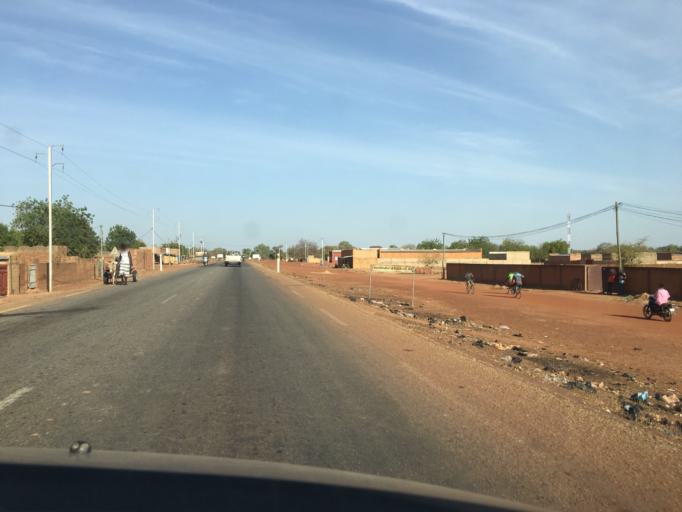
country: BF
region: Plateau-Central
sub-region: Province du Kourweogo
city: Bousse
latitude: 12.5327
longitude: -1.7791
